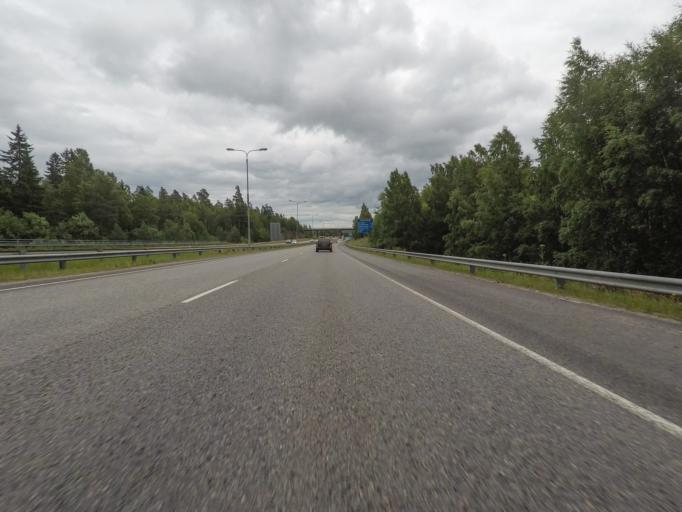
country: FI
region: Varsinais-Suomi
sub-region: Turku
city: Turku
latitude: 60.4954
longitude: 22.3026
